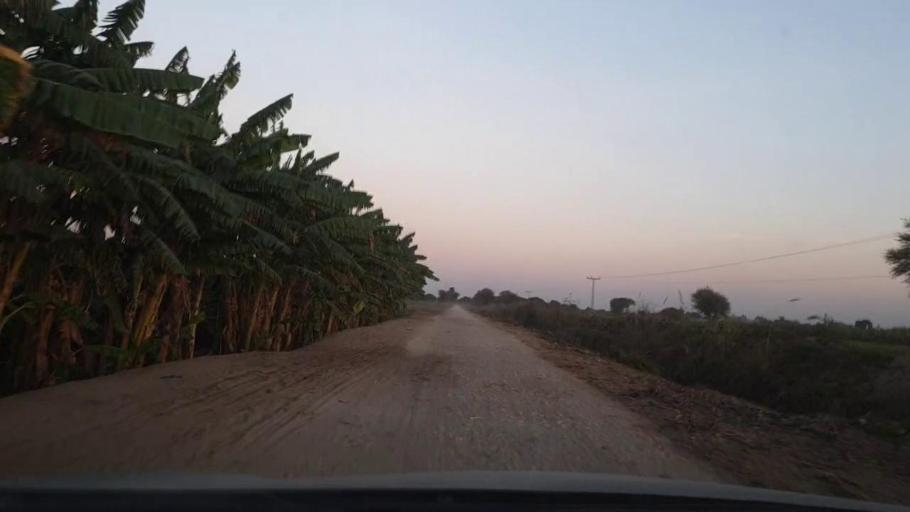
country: PK
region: Sindh
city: Tando Allahyar
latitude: 25.5573
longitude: 68.7815
